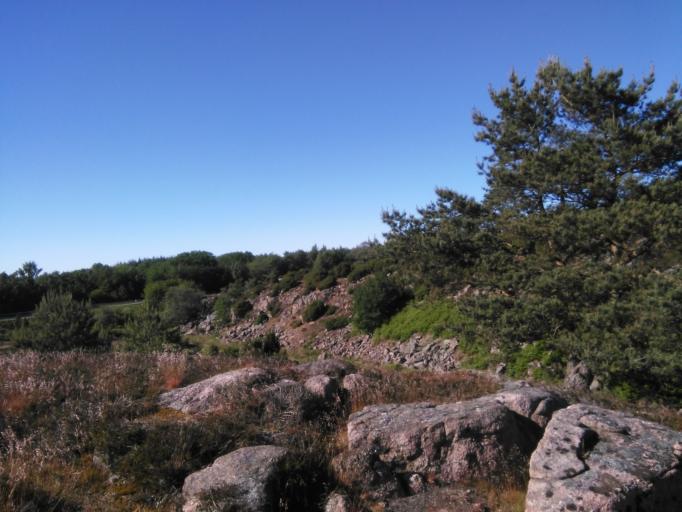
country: DK
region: Capital Region
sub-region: Bornholm Kommune
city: Ronne
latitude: 55.2610
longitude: 14.7676
